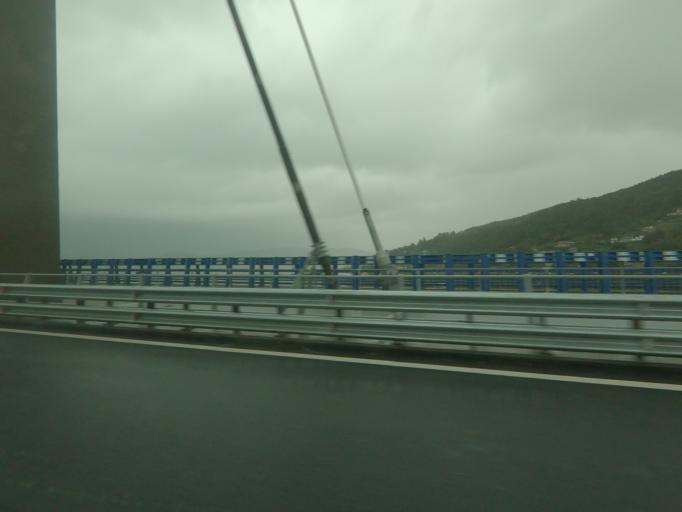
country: ES
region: Galicia
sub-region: Provincia de Pontevedra
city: Redondela
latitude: 42.2864
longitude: -8.6604
